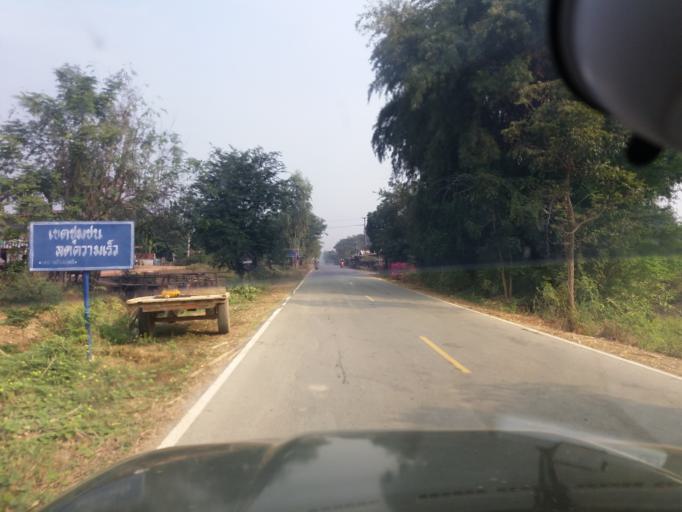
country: TH
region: Suphan Buri
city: Doem Bang Nang Buat
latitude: 14.8588
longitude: 100.1651
